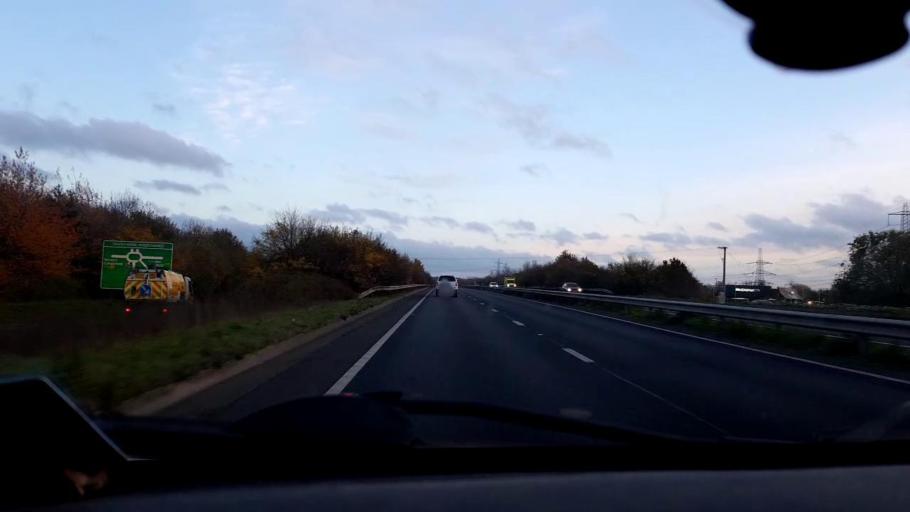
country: GB
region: England
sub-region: Norfolk
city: Cringleford
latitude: 52.6057
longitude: 1.2220
